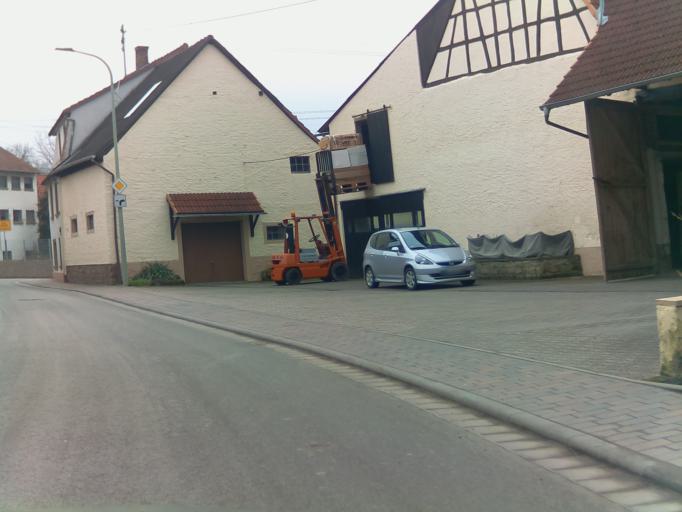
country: DE
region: Rheinland-Pfalz
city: Gerbach
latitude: 49.6745
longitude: 7.8695
